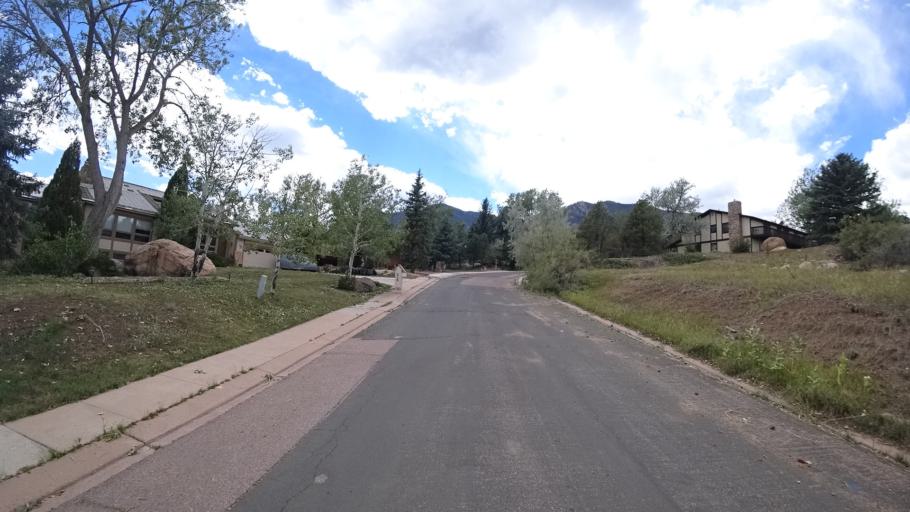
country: US
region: Colorado
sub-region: El Paso County
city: Stratmoor
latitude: 38.7726
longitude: -104.8320
